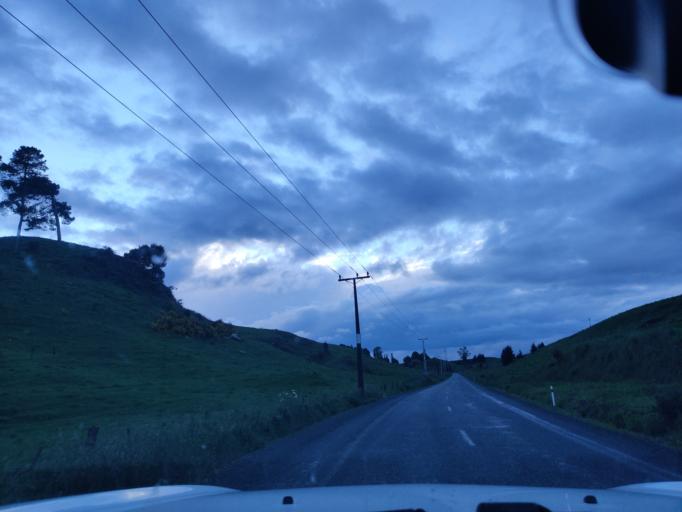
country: NZ
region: Waikato
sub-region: South Waikato District
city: Tokoroa
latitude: -38.1966
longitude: 175.8052
